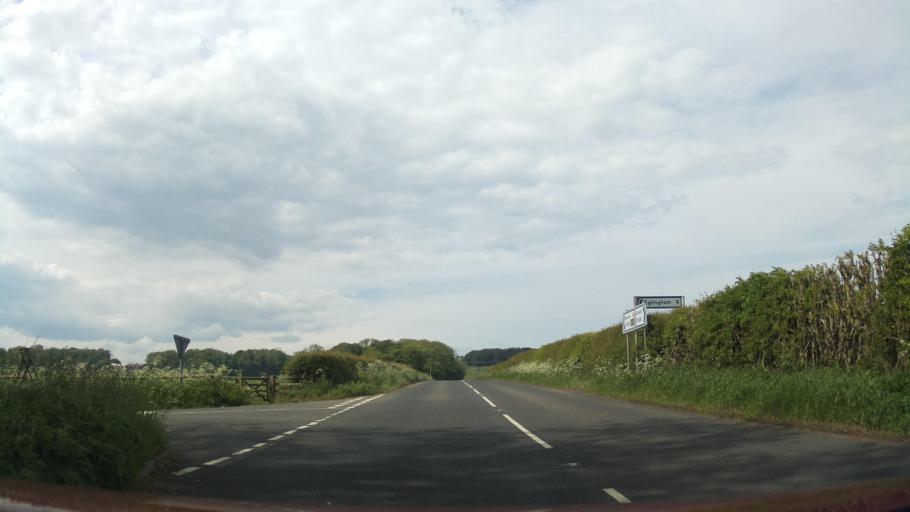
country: GB
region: England
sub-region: Northumberland
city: Alnwick
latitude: 55.4309
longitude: -1.7060
